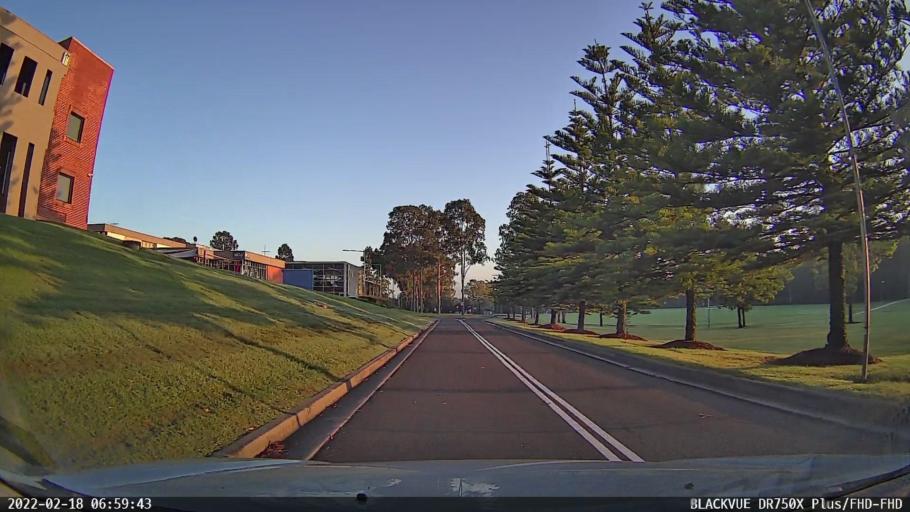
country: AU
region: New South Wales
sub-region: Penrith Municipality
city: Kingswood Park
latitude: -33.7671
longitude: 150.7303
